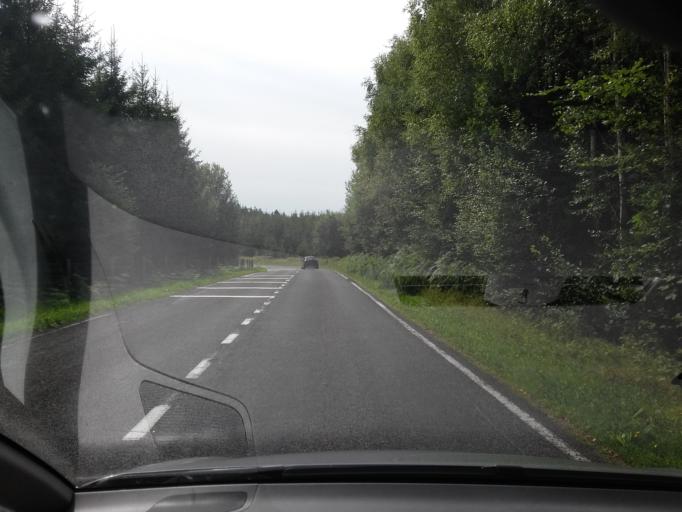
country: BE
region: Wallonia
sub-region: Province du Luxembourg
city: Chiny
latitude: 49.7830
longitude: 5.3461
